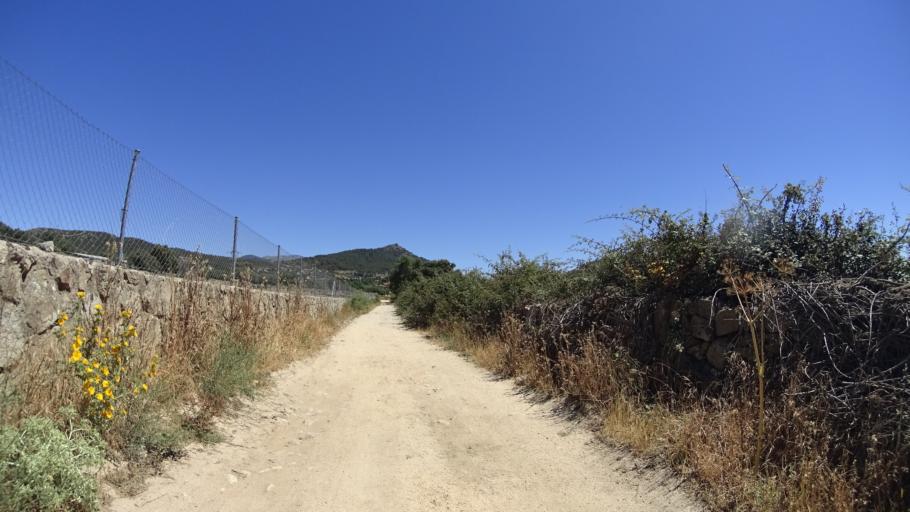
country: ES
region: Madrid
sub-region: Provincia de Madrid
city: Collado Mediano
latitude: 40.6832
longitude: -4.0371
